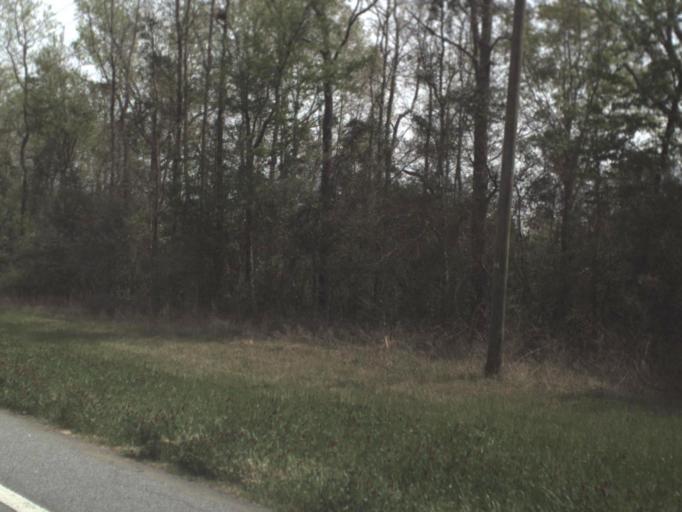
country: US
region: Alabama
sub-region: Geneva County
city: Geneva
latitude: 30.9466
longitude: -85.7558
